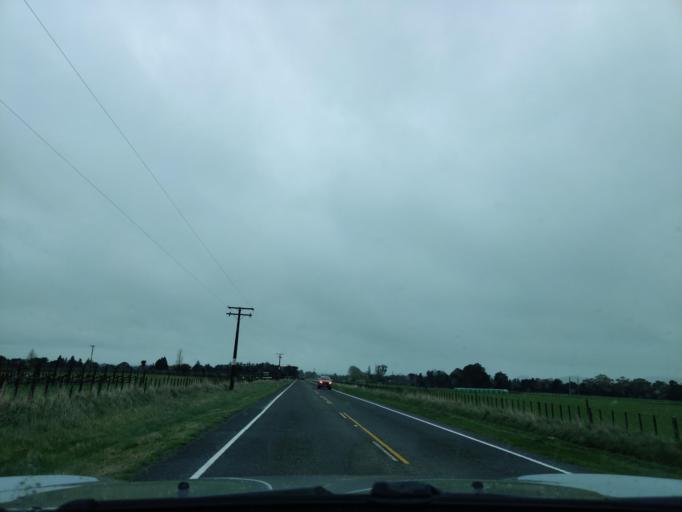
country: NZ
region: Hawke's Bay
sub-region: Hastings District
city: Hastings
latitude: -40.0208
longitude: 176.3134
